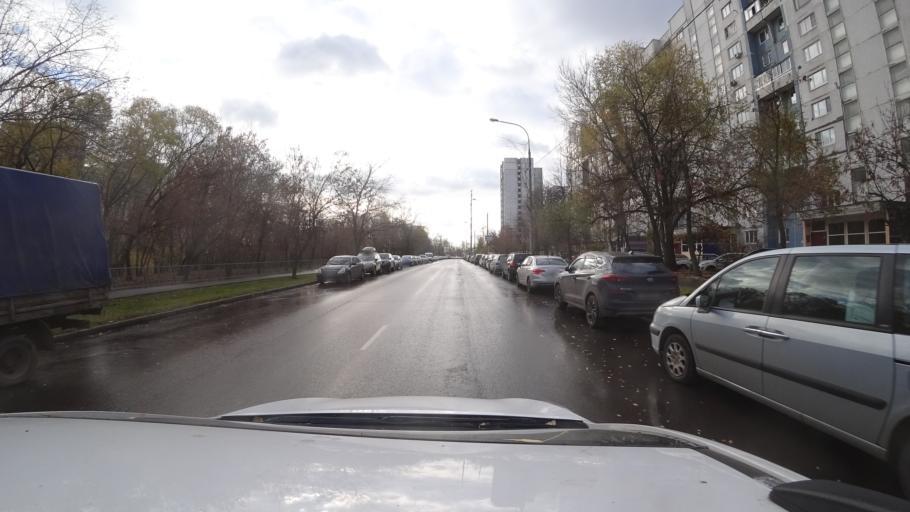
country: RU
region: Moscow
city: Zagor'ye
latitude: 55.5775
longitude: 37.6684
